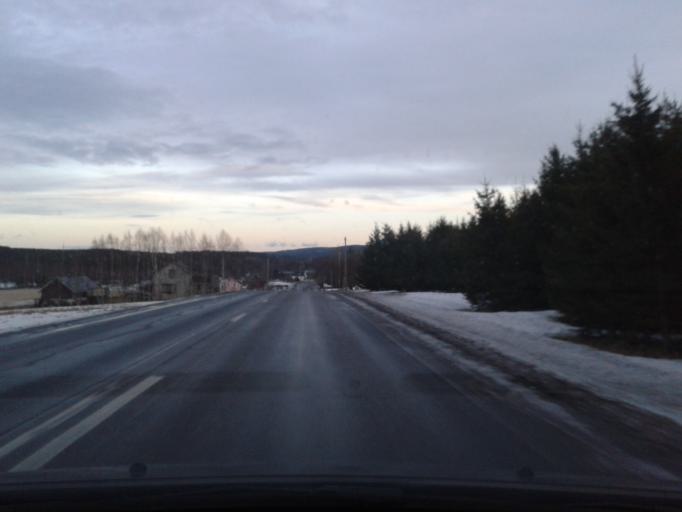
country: SE
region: Vaesternorrland
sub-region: Solleftea Kommun
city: Solleftea
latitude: 63.1487
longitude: 17.3749
